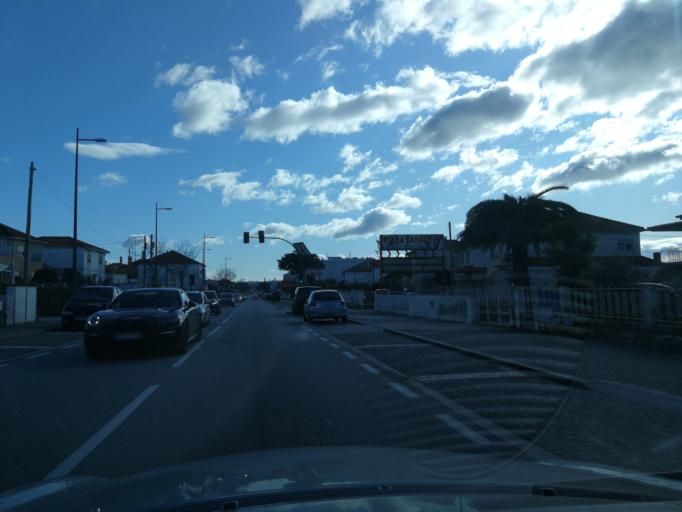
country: PT
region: Viana do Castelo
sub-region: Viana do Castelo
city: Viana do Castelo
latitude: 41.6987
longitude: -8.8454
